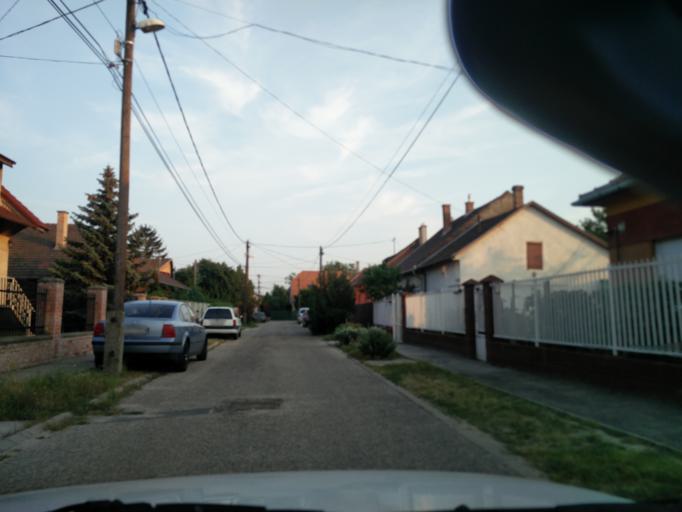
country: HU
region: Budapest
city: Budapest XXIII. keruelet
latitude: 47.4036
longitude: 19.0852
